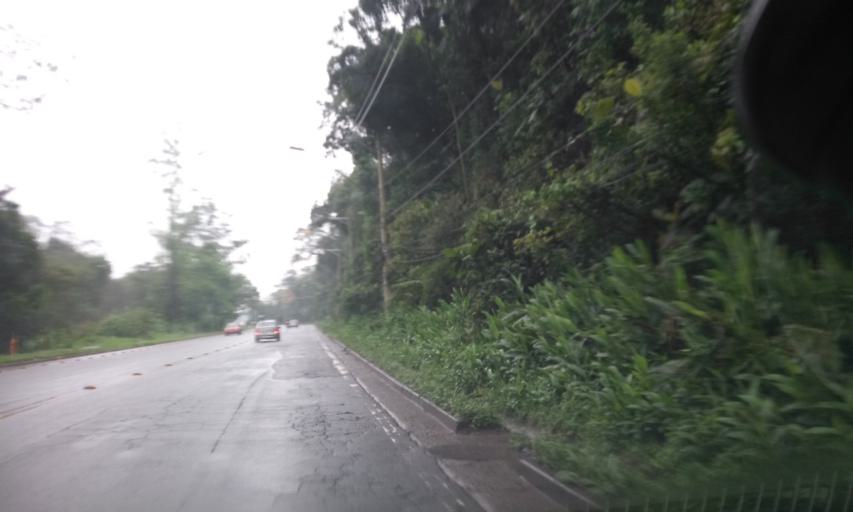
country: BR
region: Sao Paulo
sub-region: Maua
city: Maua
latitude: -23.7160
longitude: -46.4990
